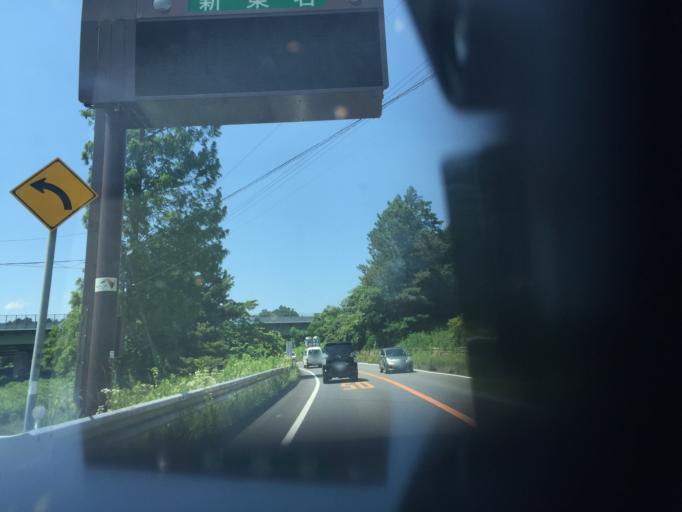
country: JP
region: Shizuoka
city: Mori
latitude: 34.8257
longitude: 137.9495
